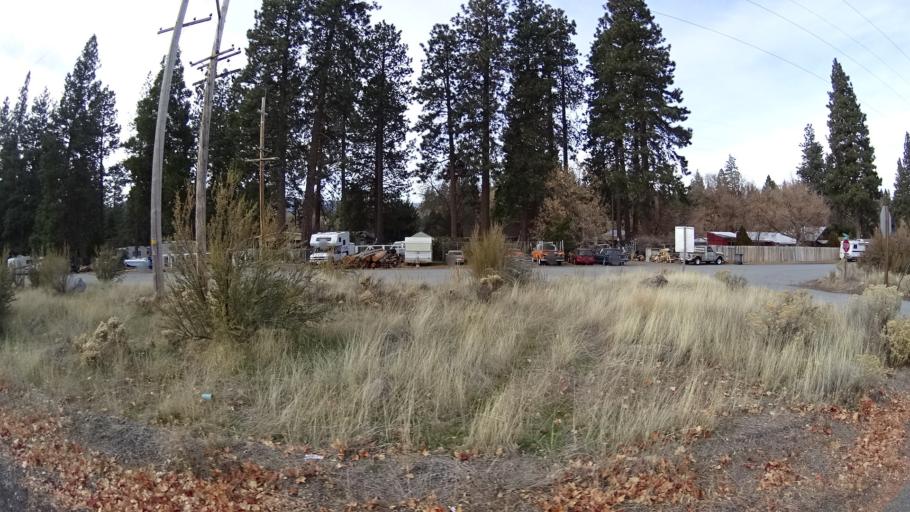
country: US
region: California
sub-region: Siskiyou County
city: Weed
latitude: 41.4476
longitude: -122.3619
